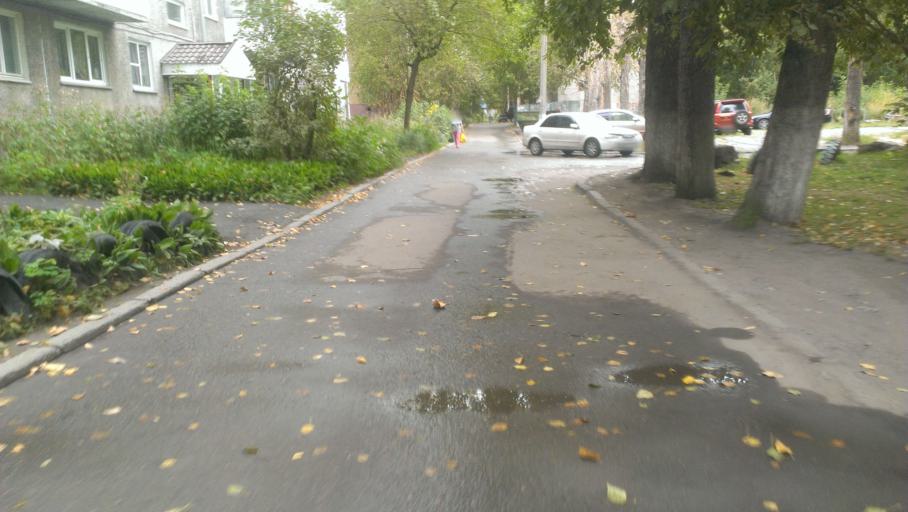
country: RU
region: Altai Krai
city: Novosilikatnyy
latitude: 53.3732
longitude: 83.6723
